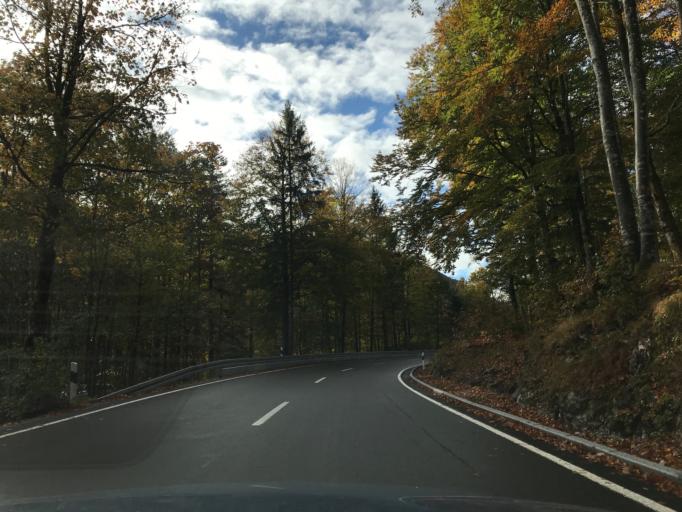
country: DE
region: Bavaria
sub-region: Upper Bavaria
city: Lenggries
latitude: 47.5813
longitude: 11.5471
